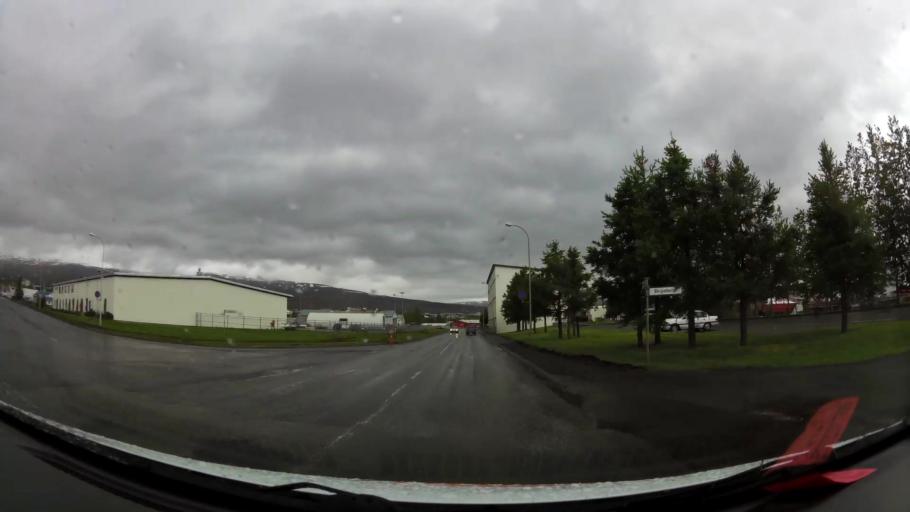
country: IS
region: Northeast
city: Akureyri
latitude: 65.6915
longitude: -18.0922
